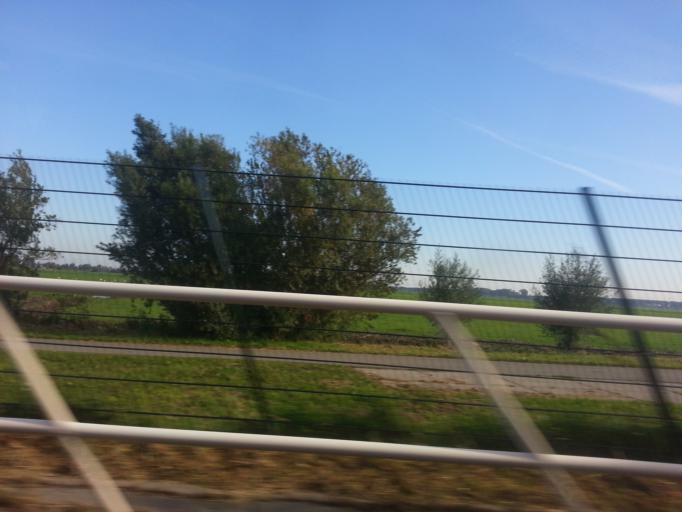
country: NL
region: North Holland
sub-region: Gemeente Amsterdam
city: Amsterdam-Zuidoost
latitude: 52.2713
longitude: 4.9842
